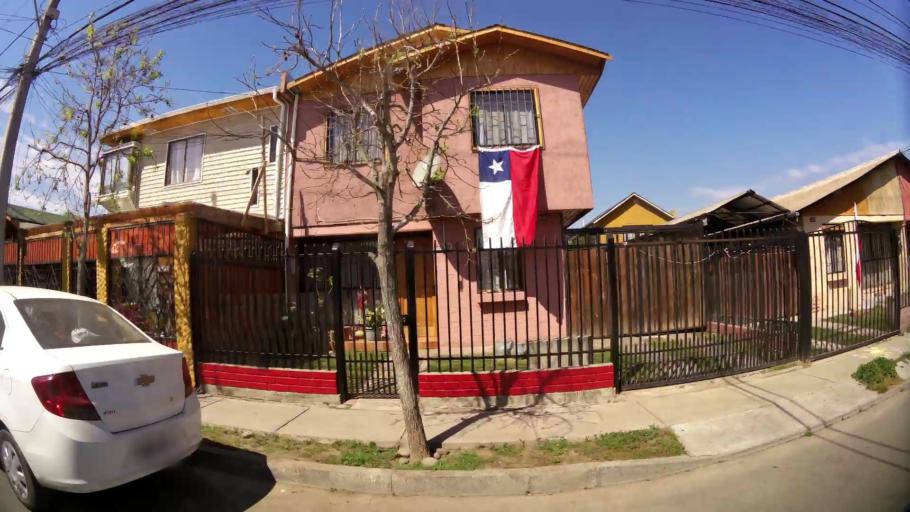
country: CL
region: Santiago Metropolitan
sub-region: Provincia de Talagante
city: Talagante
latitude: -33.6557
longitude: -70.9128
